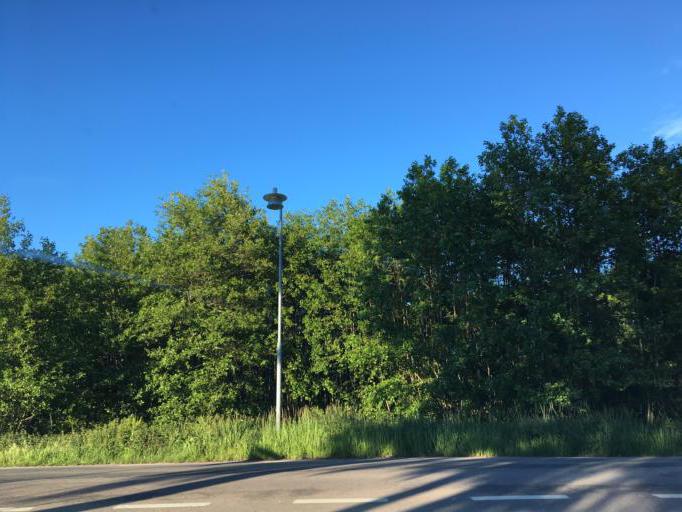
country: SE
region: Vaestmanland
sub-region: Vasteras
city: Vasteras
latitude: 59.5189
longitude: 16.5290
